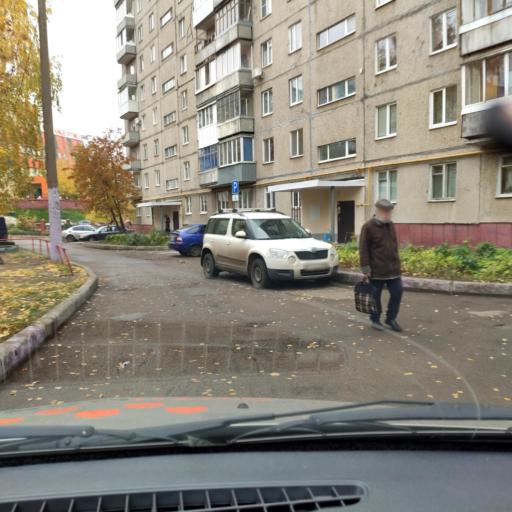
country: RU
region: Bashkortostan
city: Ufa
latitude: 54.7011
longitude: 55.9865
